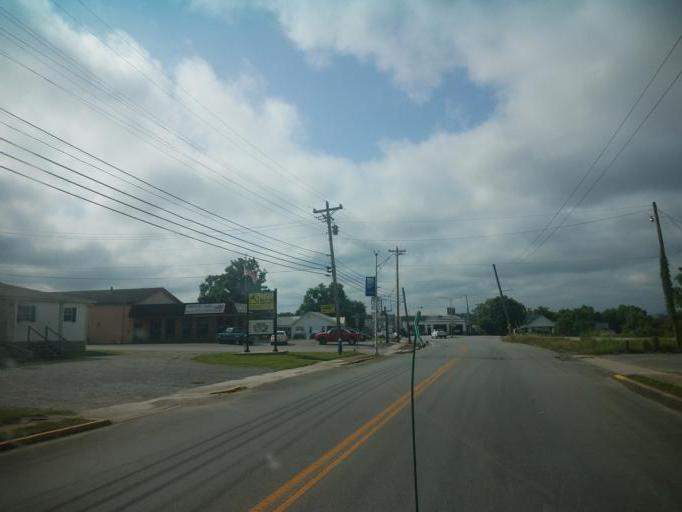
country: US
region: Kentucky
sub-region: Clinton County
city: Albany
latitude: 36.6851
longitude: -85.1324
